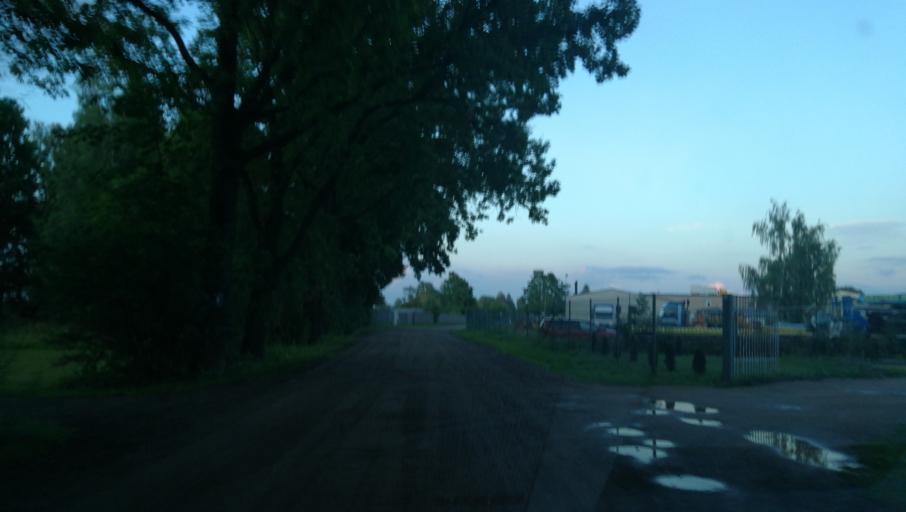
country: LV
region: Cesu Rajons
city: Cesis
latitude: 57.3138
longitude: 25.3022
